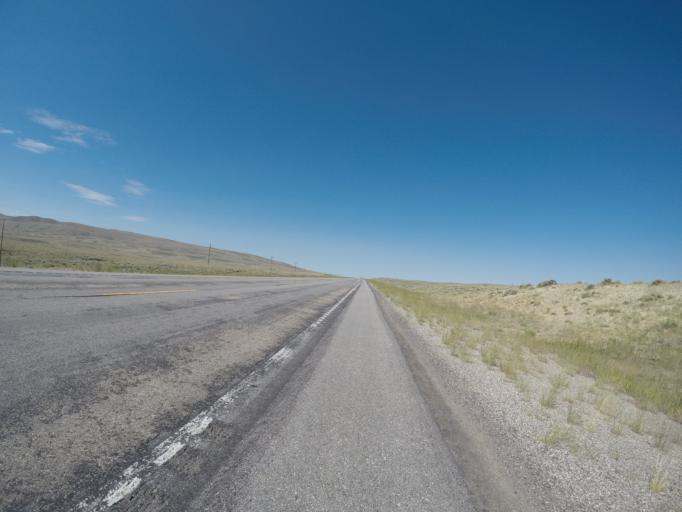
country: US
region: Wyoming
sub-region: Carbon County
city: Saratoga
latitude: 41.8016
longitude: -106.7077
